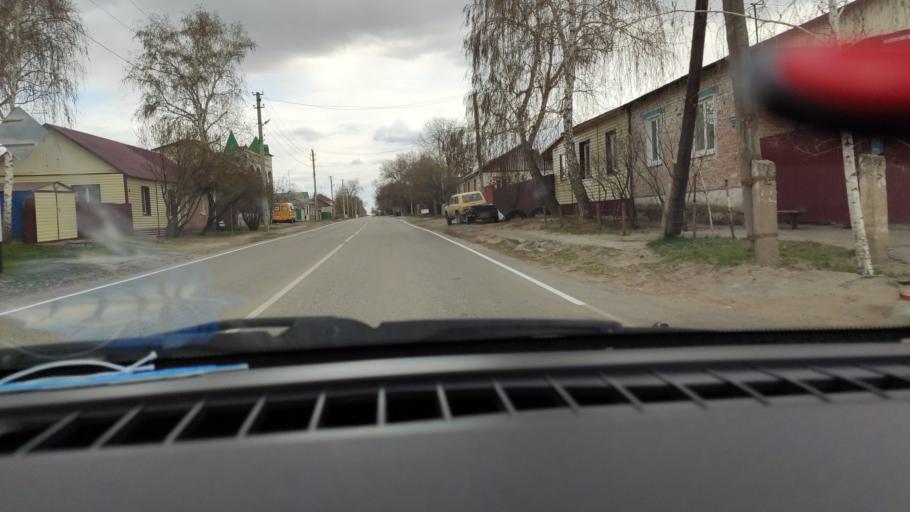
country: RU
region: Saratov
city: Privolzhskiy
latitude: 51.1855
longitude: 45.9176
